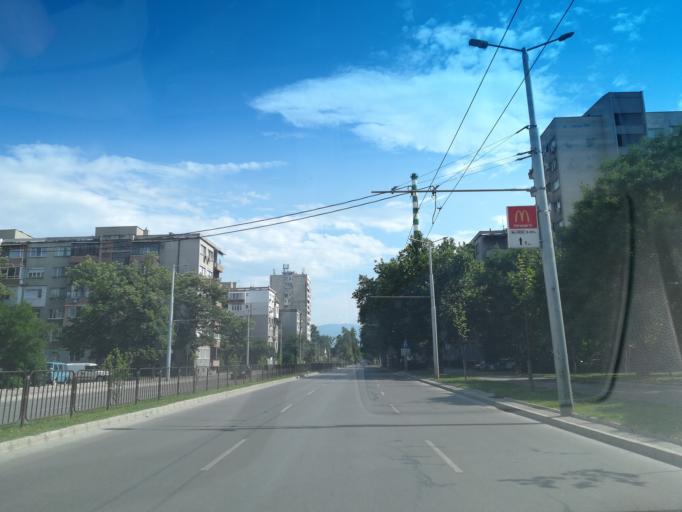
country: BG
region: Plovdiv
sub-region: Obshtina Plovdiv
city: Plovdiv
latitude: 42.1456
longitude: 24.7631
